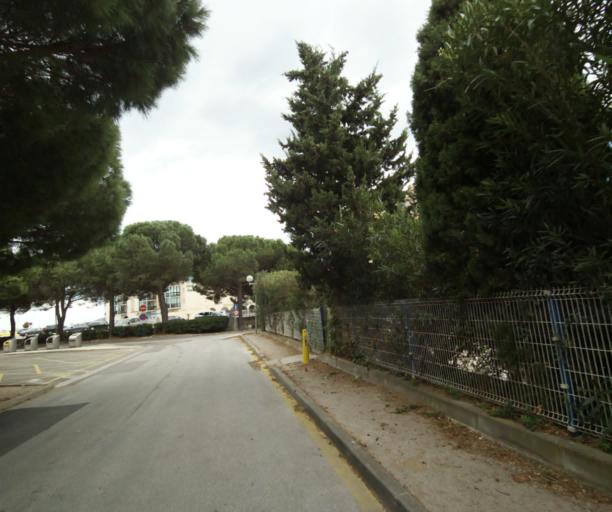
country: FR
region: Languedoc-Roussillon
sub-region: Departement des Pyrenees-Orientales
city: Argelers
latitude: 42.5431
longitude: 3.0499
